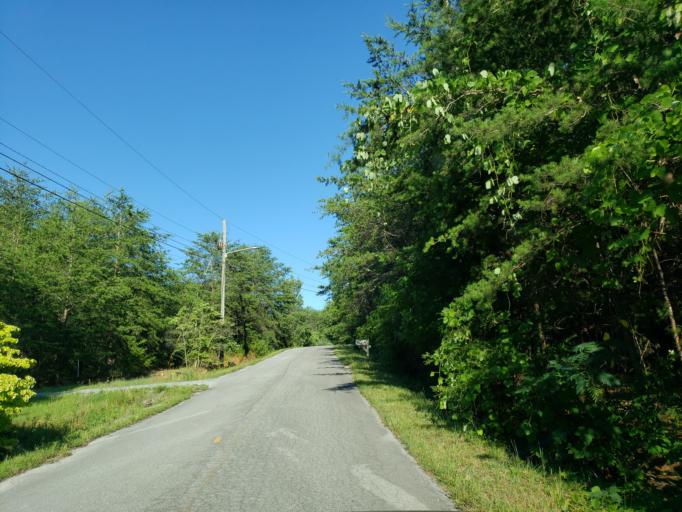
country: US
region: Georgia
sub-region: Polk County
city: Aragon
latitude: 34.0882
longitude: -84.9968
